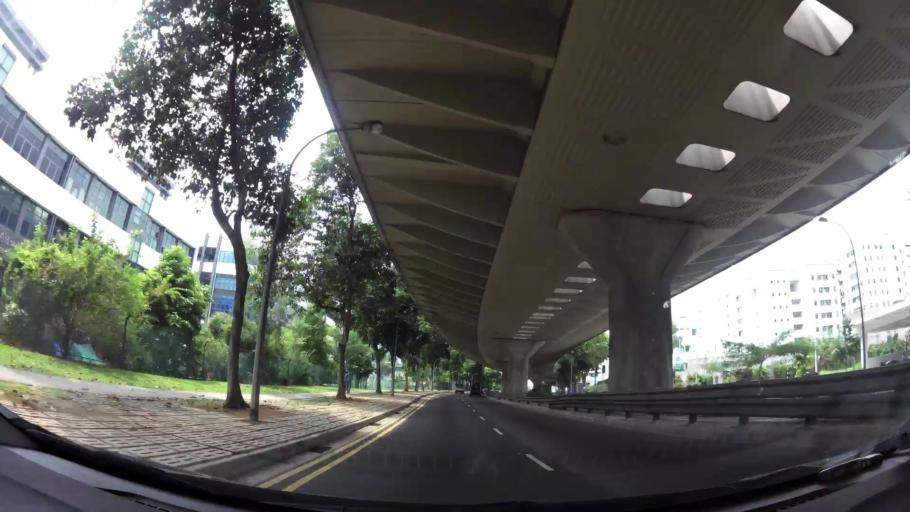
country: SG
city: Singapore
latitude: 1.3380
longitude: 103.9109
